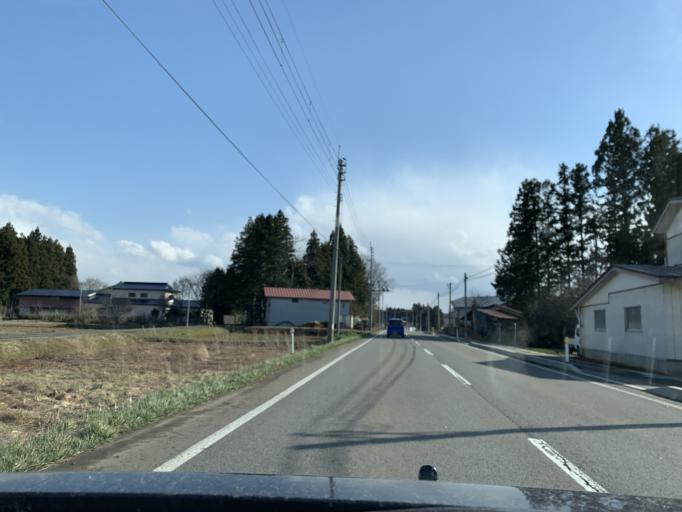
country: JP
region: Iwate
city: Mizusawa
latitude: 39.1050
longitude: 141.0519
